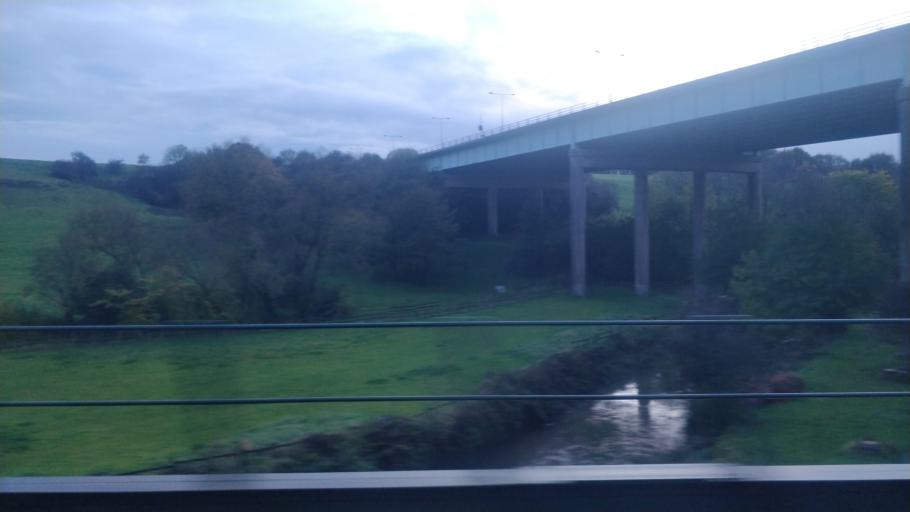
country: GB
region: England
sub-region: Borough of Wigan
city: Shevington
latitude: 53.5611
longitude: -2.7002
